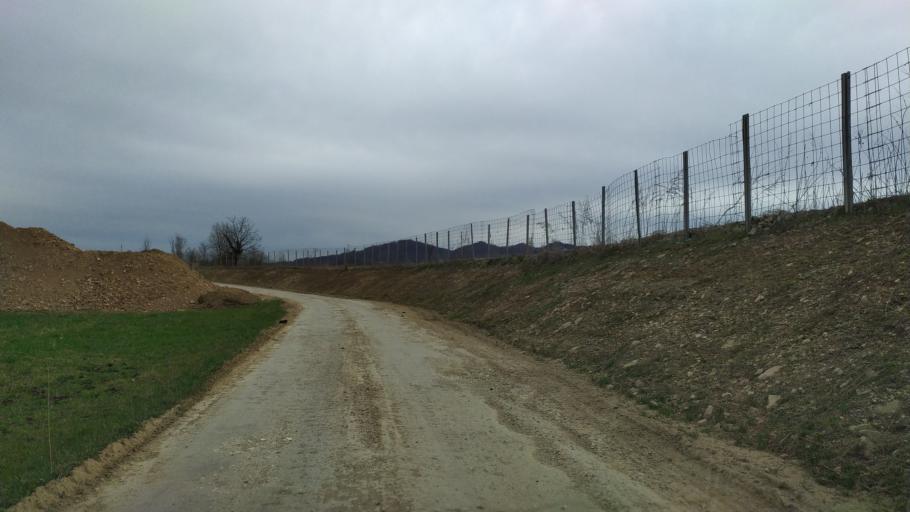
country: IT
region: Veneto
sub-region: Provincia di Vicenza
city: Malo
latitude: 45.6543
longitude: 11.4354
